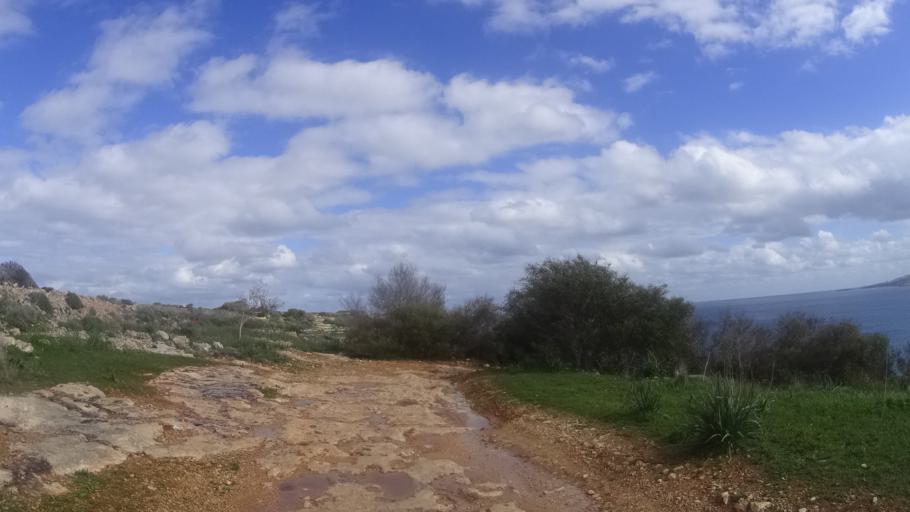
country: MT
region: Il-Mellieha
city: Mellieha
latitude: 35.9801
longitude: 14.3591
